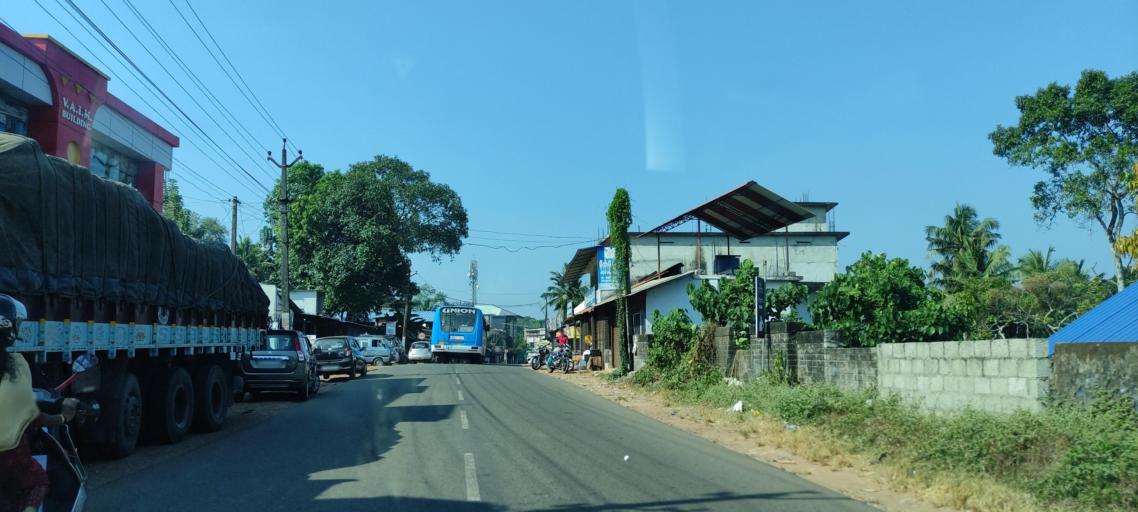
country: IN
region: Kerala
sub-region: Kollam
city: Panmana
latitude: 9.0620
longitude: 76.6407
